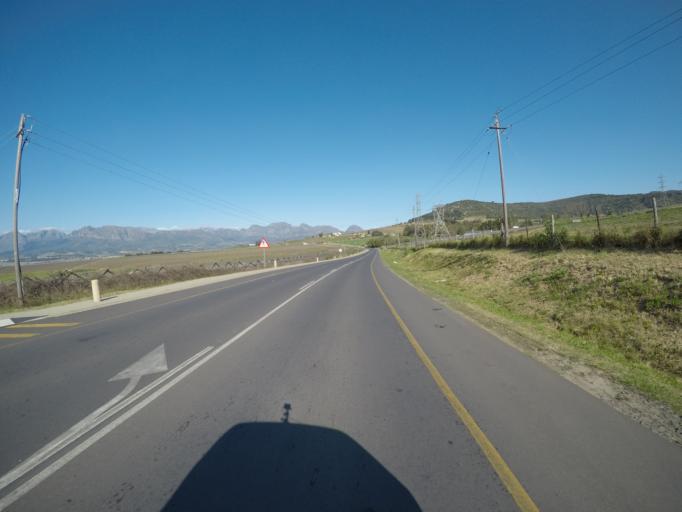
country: ZA
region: Western Cape
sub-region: Cape Winelands District Municipality
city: Noorder-Paarl
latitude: -33.6728
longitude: 18.9318
